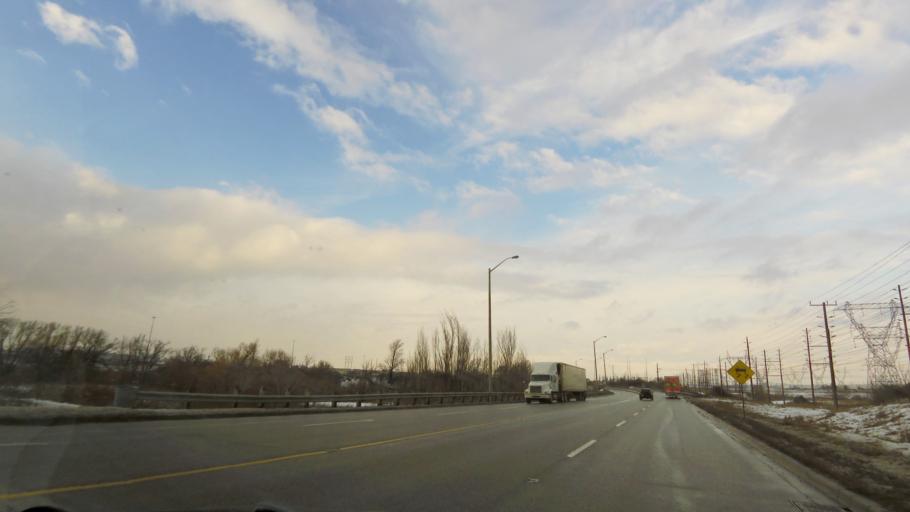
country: CA
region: Ontario
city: Brampton
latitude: 43.6752
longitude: -79.6912
